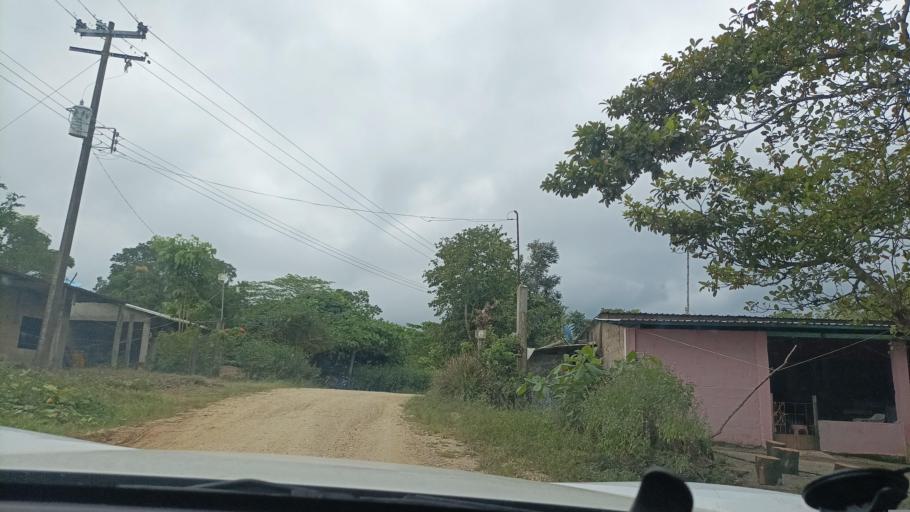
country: MX
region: Veracruz
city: Hidalgotitlan
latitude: 17.6437
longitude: -94.5107
